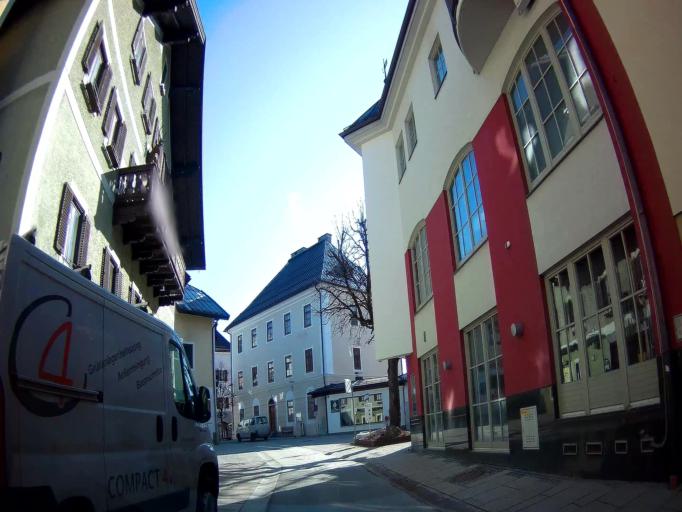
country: AT
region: Salzburg
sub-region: Politischer Bezirk Zell am See
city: Saalfelden am Steinernen Meer
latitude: 47.4277
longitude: 12.8481
